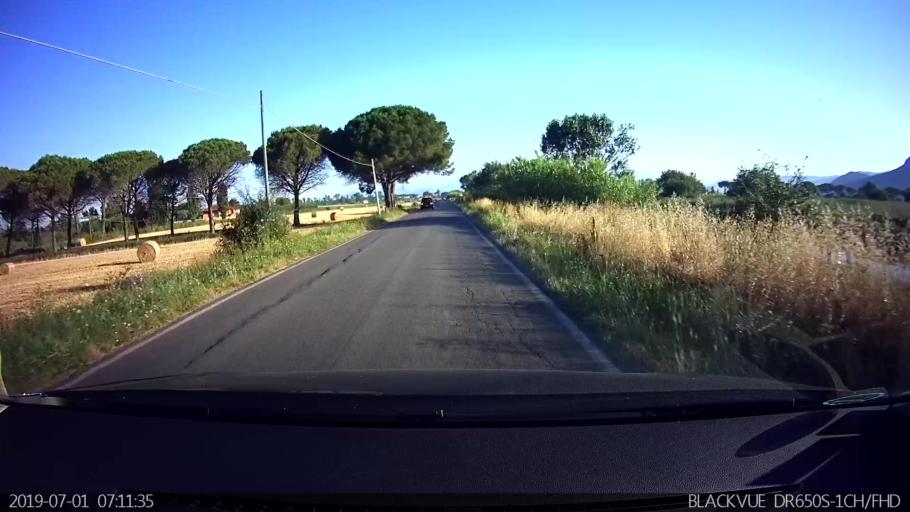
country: IT
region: Latium
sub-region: Provincia di Latina
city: Borgo Hermada
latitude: 41.3213
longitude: 13.1777
